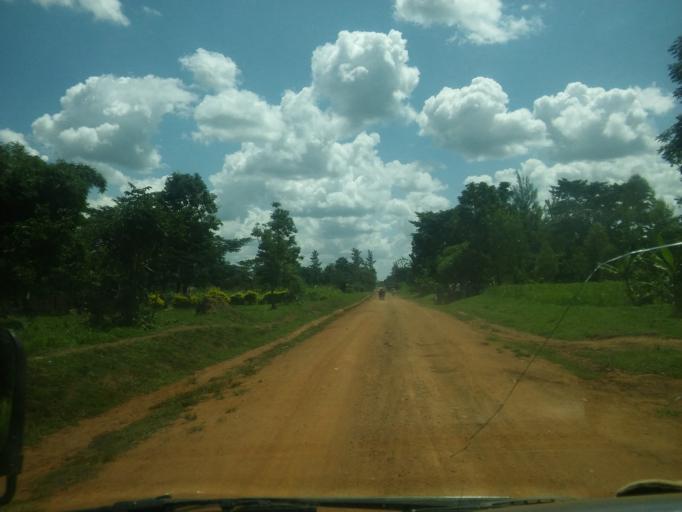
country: UG
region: Eastern Region
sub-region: Kibuku District
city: Kibuku
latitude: 1.1365
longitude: 33.8637
